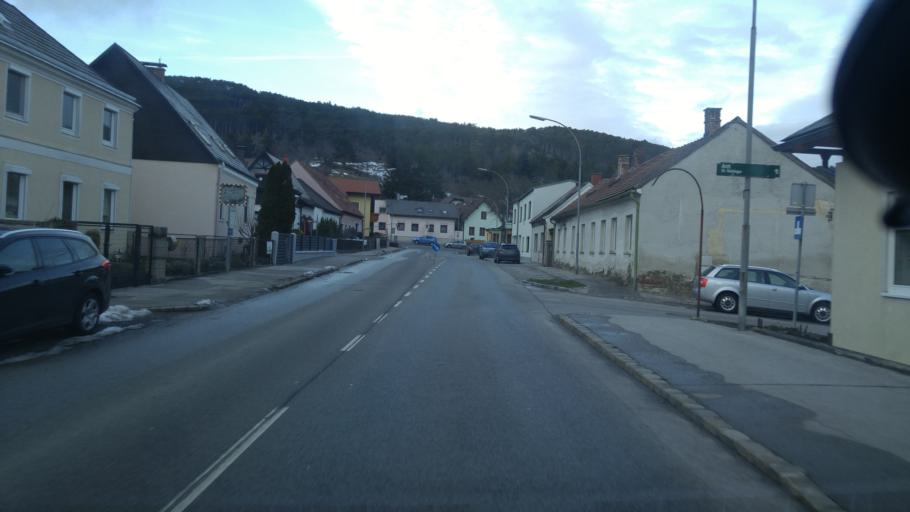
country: AT
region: Lower Austria
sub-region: Politischer Bezirk Baden
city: Bad Voslau
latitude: 47.9619
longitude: 16.1921
